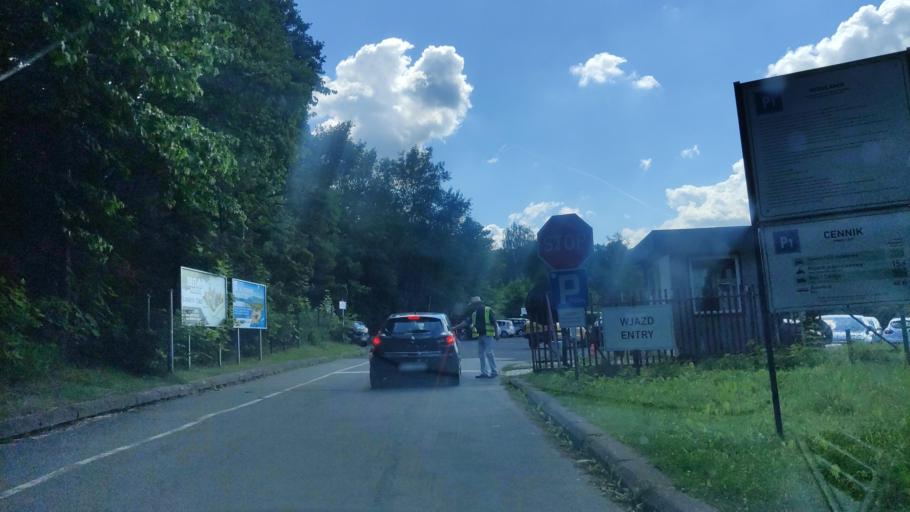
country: PL
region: Lower Silesian Voivodeship
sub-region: Powiat swidnicki
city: Swiebodzice
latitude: 50.8383
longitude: 16.3007
